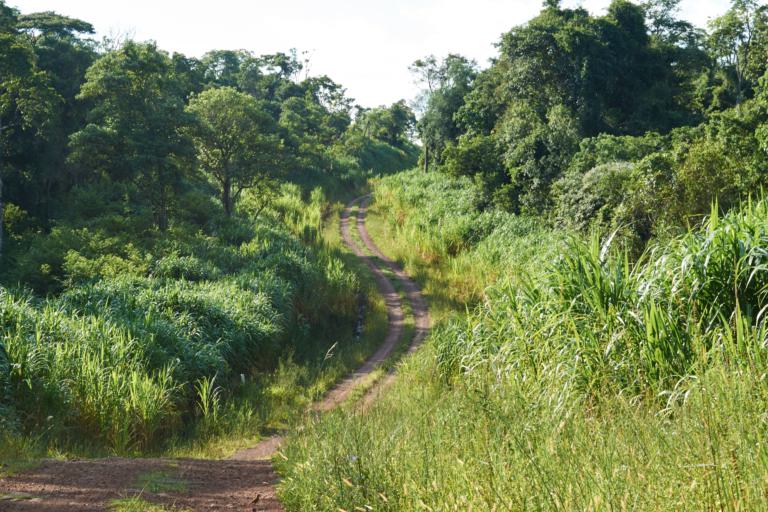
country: AR
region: Misiones
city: Dos de Mayo
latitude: -26.8415
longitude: -54.6185
